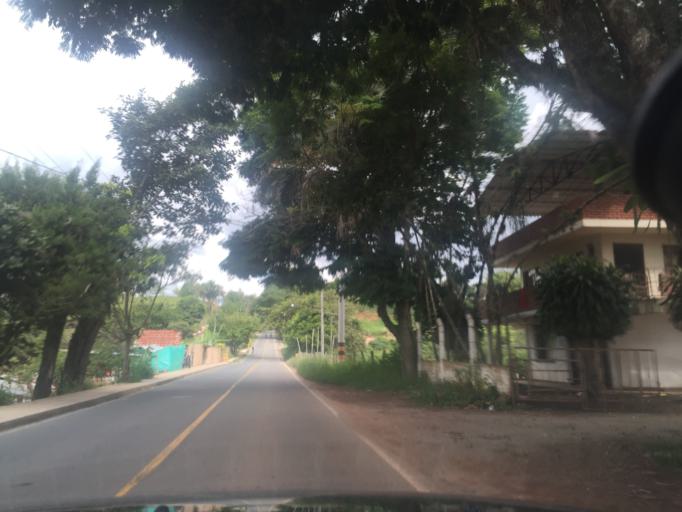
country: CO
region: Valle del Cauca
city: Caicedonia
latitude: 4.3410
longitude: -75.8427
